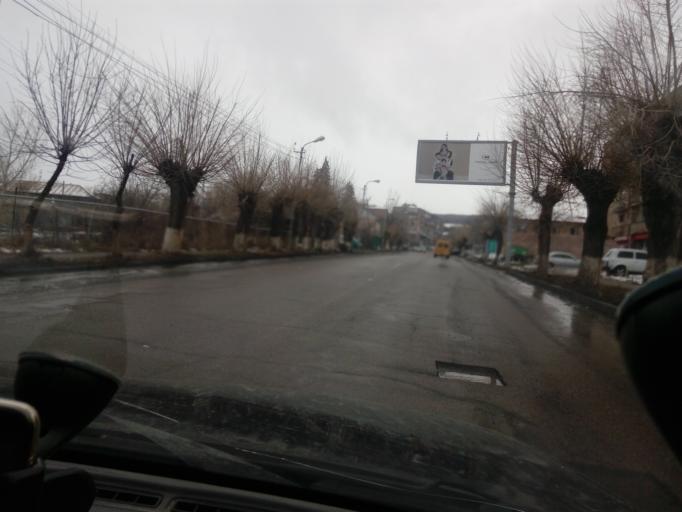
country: AM
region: Kotayk'i Marz
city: Hrazdan
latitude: 40.5001
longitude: 44.7546
